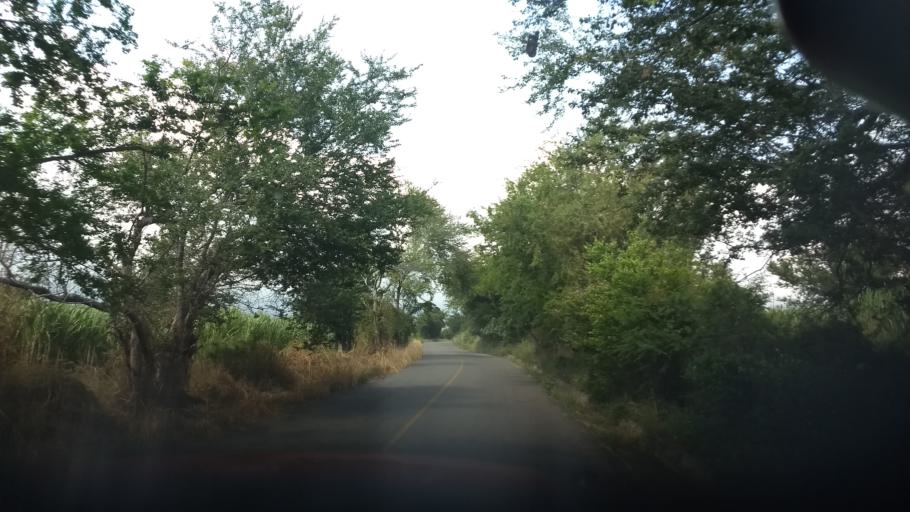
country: MX
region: Jalisco
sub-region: Tonila
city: San Marcos
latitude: 19.4289
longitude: -103.4920
